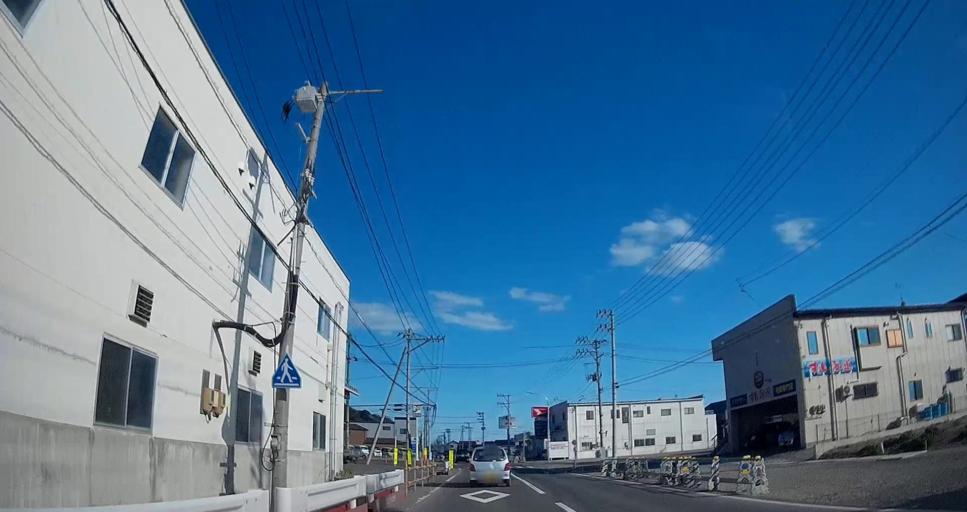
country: JP
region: Miyagi
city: Ishinomaki
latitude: 38.4245
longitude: 141.3180
